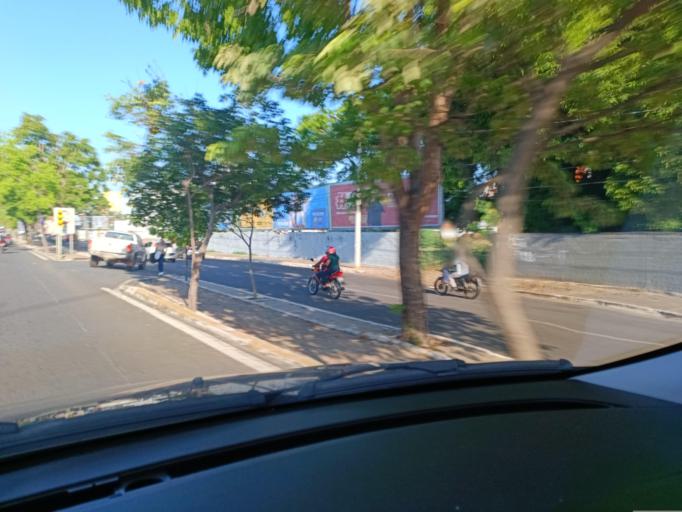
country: BR
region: Piaui
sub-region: Teresina
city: Teresina
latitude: -5.0806
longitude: -42.7821
